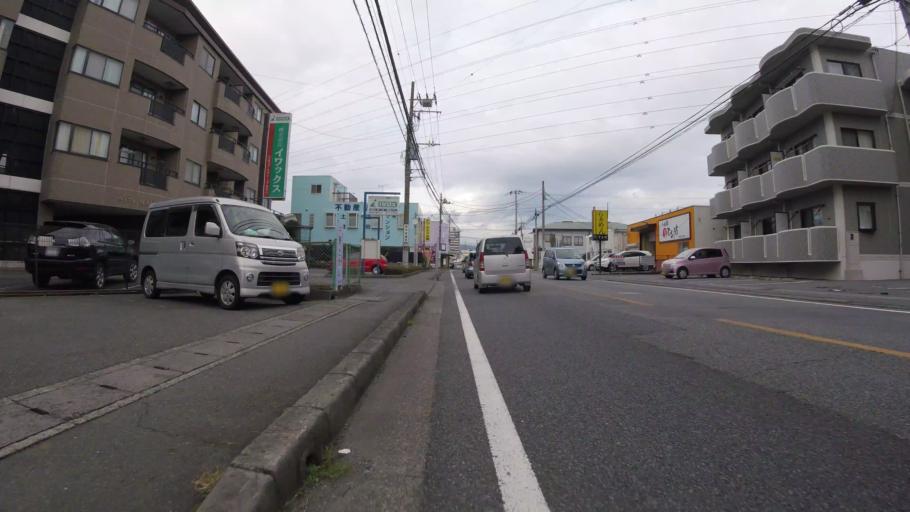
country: JP
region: Shizuoka
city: Numazu
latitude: 35.1053
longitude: 138.8919
